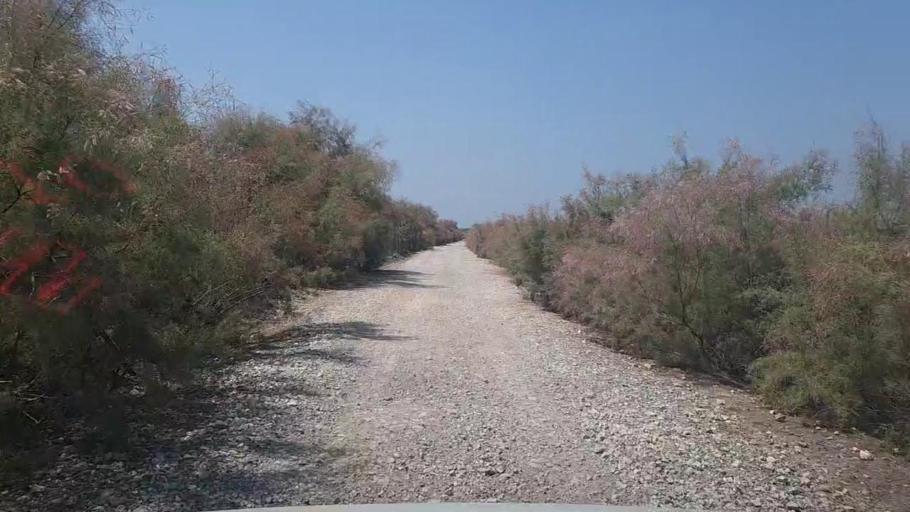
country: PK
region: Sindh
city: Kandhkot
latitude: 28.3029
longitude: 69.3534
